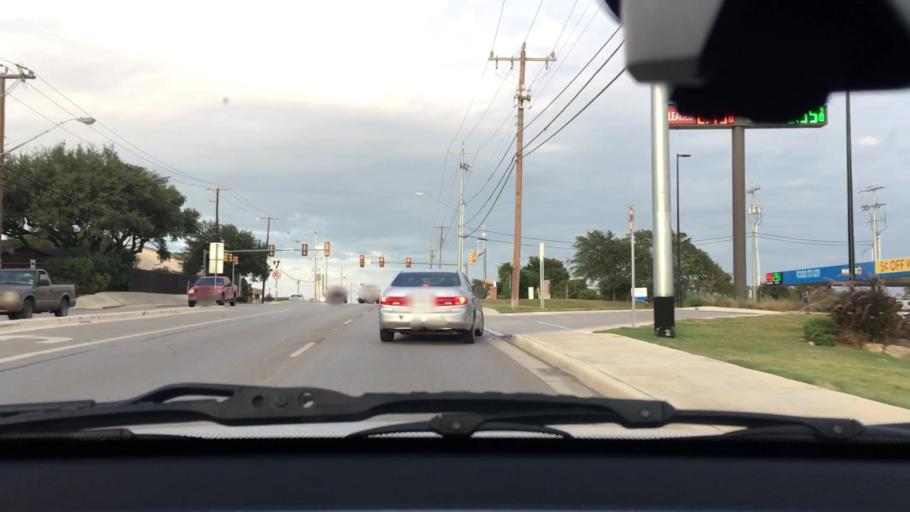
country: US
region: Texas
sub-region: Bexar County
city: Universal City
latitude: 29.5497
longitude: -98.3093
